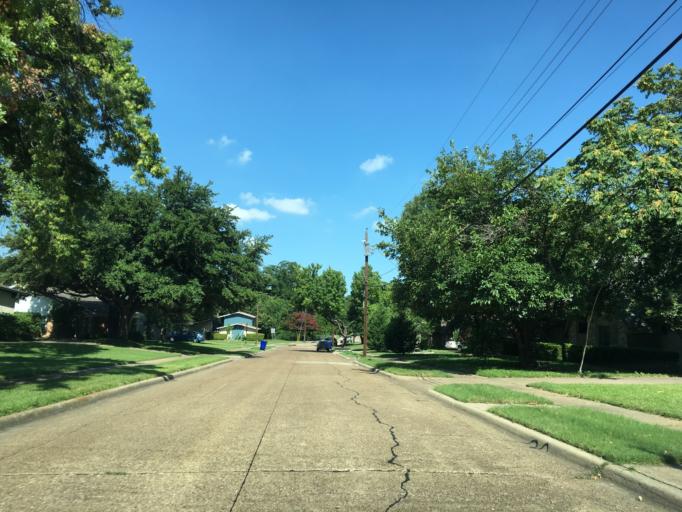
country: US
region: Texas
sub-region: Dallas County
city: Farmers Branch
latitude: 32.9171
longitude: -96.8764
